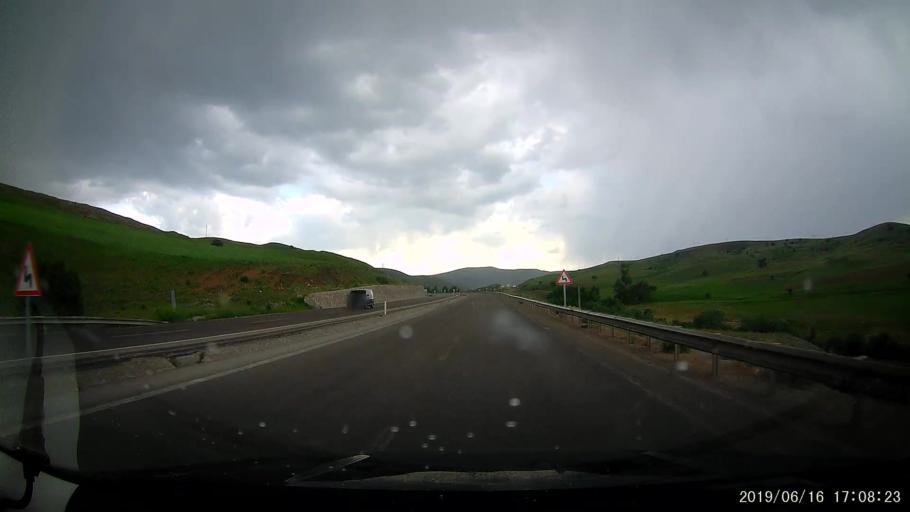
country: TR
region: Erzurum
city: Askale
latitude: 39.9098
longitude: 40.6616
